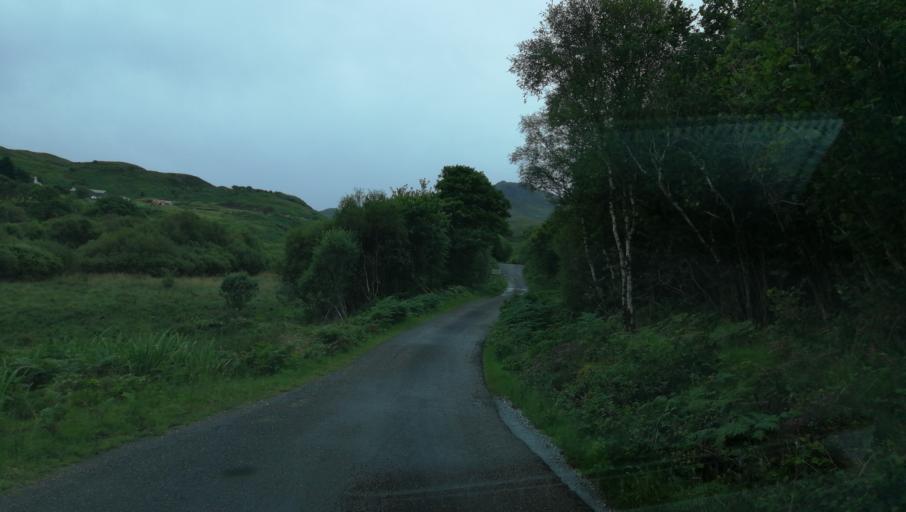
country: GB
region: Scotland
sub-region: Argyll and Bute
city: Isle Of Mull
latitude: 56.7221
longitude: -6.1707
